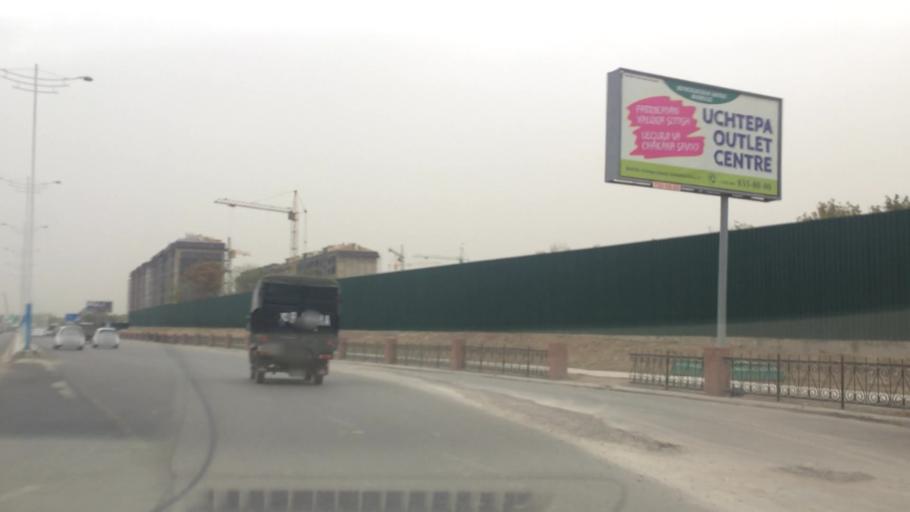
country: UZ
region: Toshkent
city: Salor
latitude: 41.3056
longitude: 69.3345
